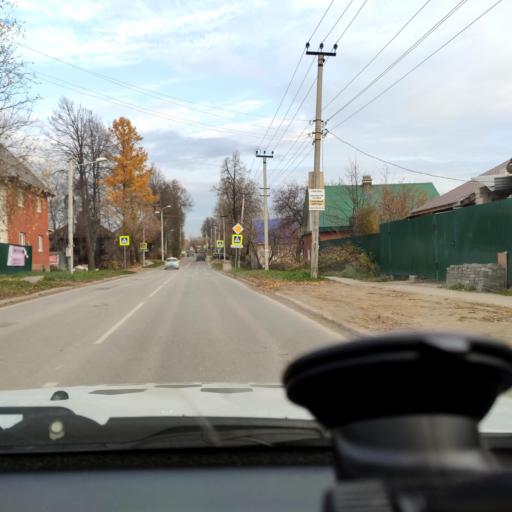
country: RU
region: Perm
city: Perm
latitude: 58.0230
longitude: 56.3362
